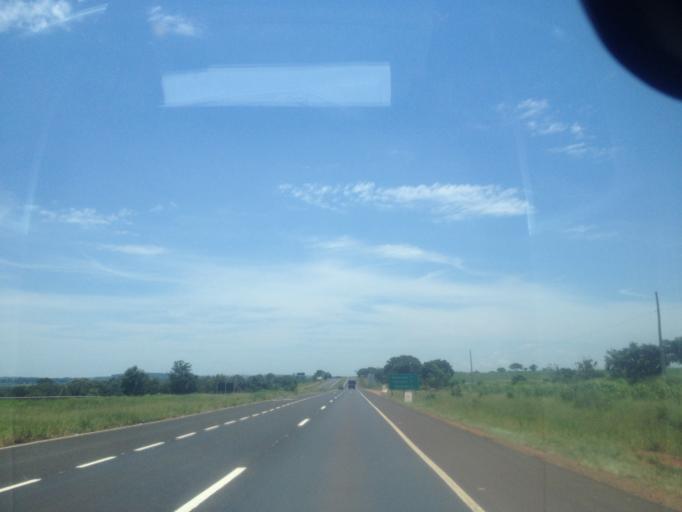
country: BR
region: Minas Gerais
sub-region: Monte Alegre De Minas
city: Monte Alegre de Minas
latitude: -18.8775
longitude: -48.9274
